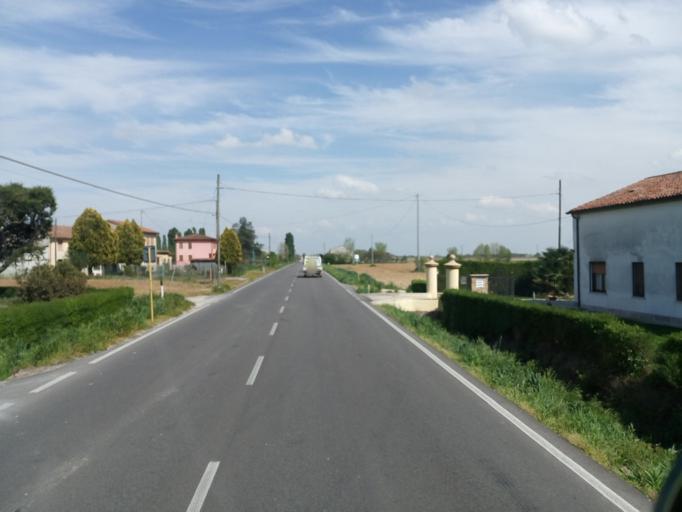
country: IT
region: Veneto
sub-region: Provincia di Verona
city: Nogara
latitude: 45.1809
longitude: 11.0963
